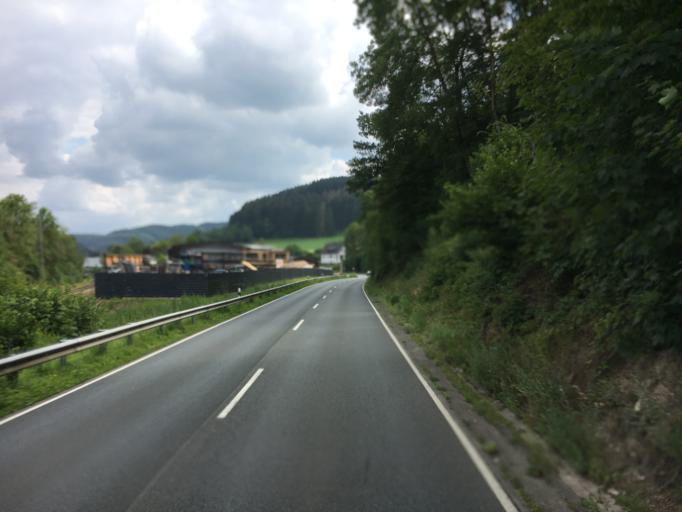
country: DE
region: North Rhine-Westphalia
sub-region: Regierungsbezirk Arnsberg
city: Lennestadt
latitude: 51.1324
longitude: 8.0277
